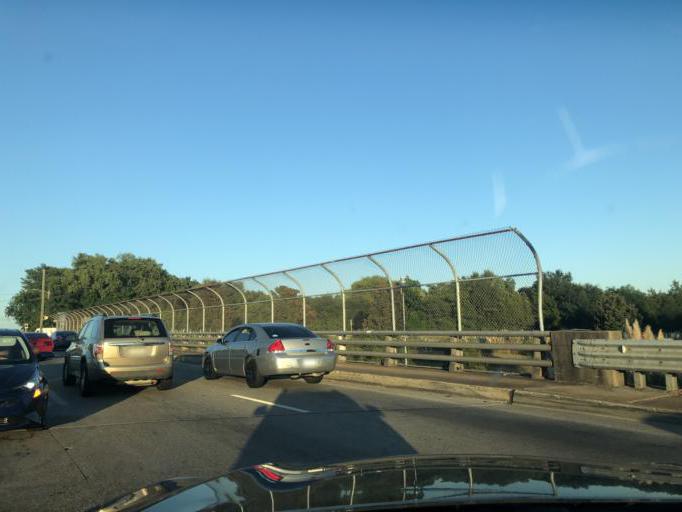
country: US
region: Georgia
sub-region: Muscogee County
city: Columbus
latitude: 32.4621
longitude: -84.9297
